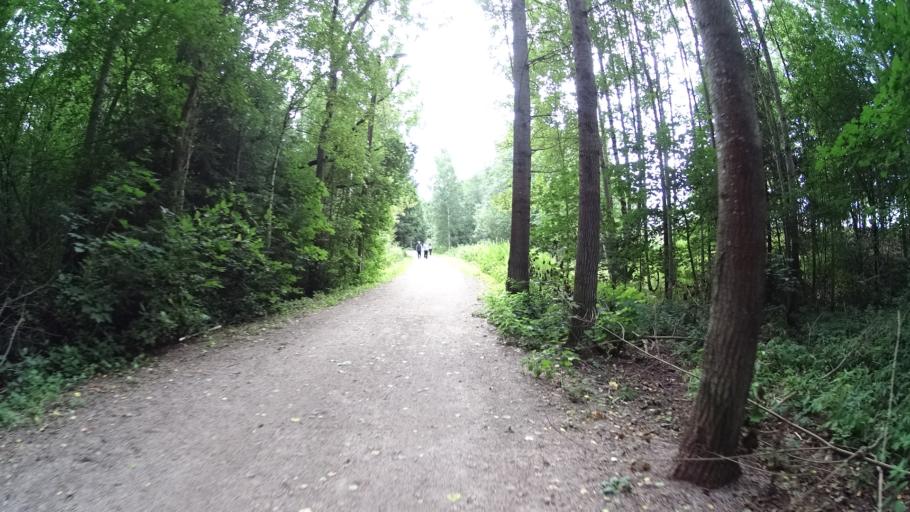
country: FI
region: Uusimaa
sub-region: Helsinki
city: Teekkarikylae
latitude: 60.2660
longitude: 24.8993
